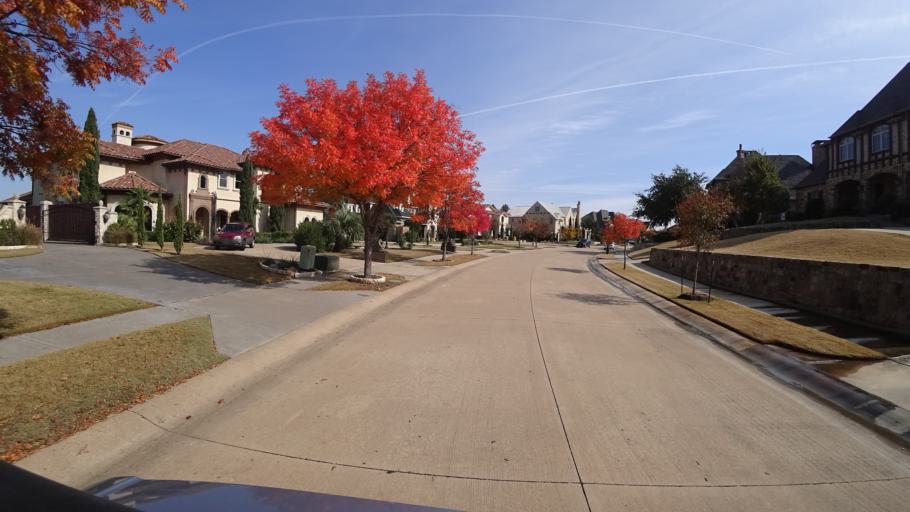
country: US
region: Texas
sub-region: Denton County
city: The Colony
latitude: 33.0417
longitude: -96.8941
